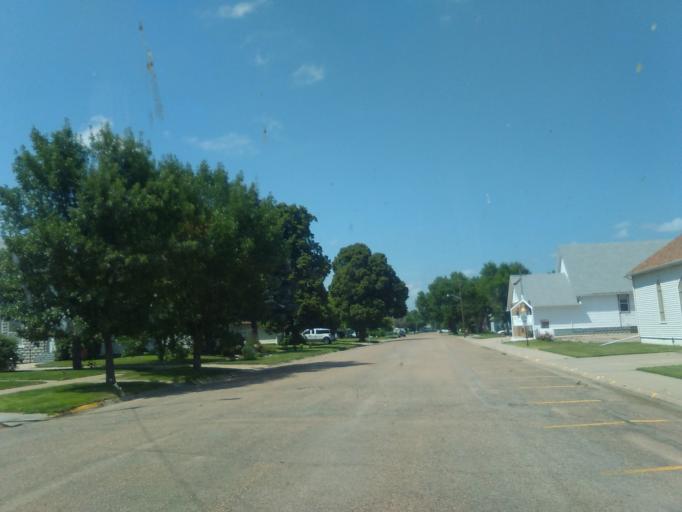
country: US
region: Nebraska
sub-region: Phelps County
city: Holdrege
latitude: 40.7194
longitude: -99.3732
